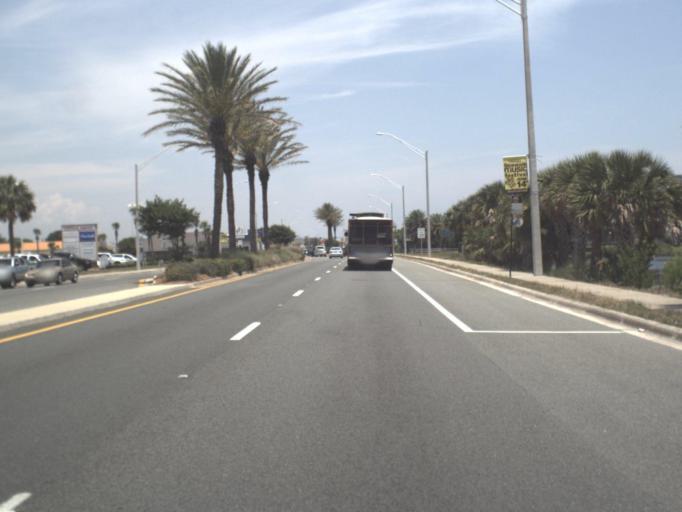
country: US
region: Florida
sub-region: Duval County
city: Jacksonville Beach
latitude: 30.2695
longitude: -81.3885
